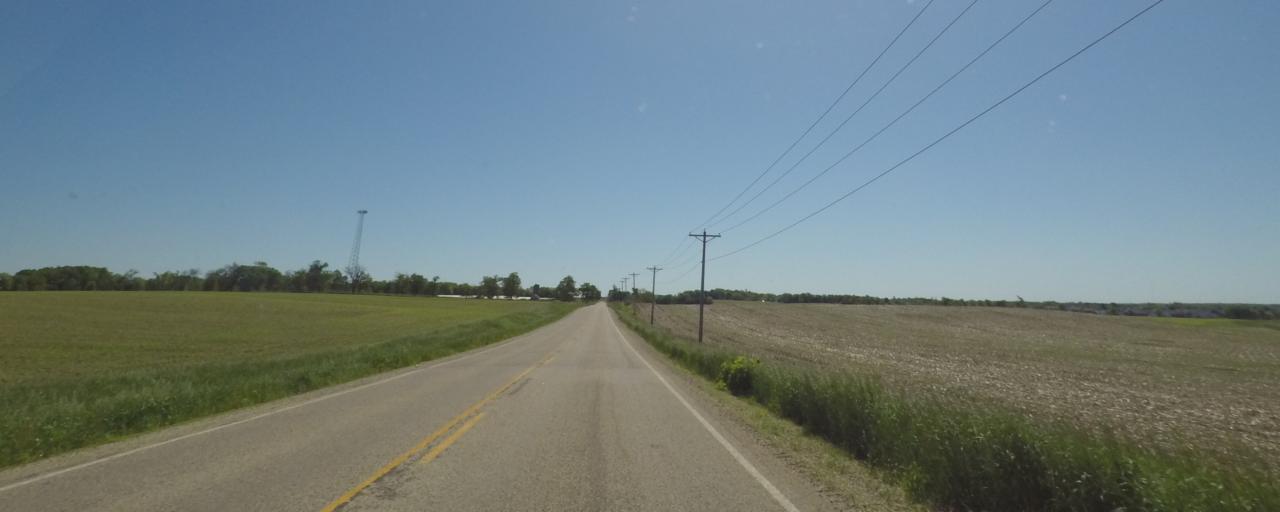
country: US
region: Wisconsin
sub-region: Rock County
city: Evansville
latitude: 42.7876
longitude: -89.3335
